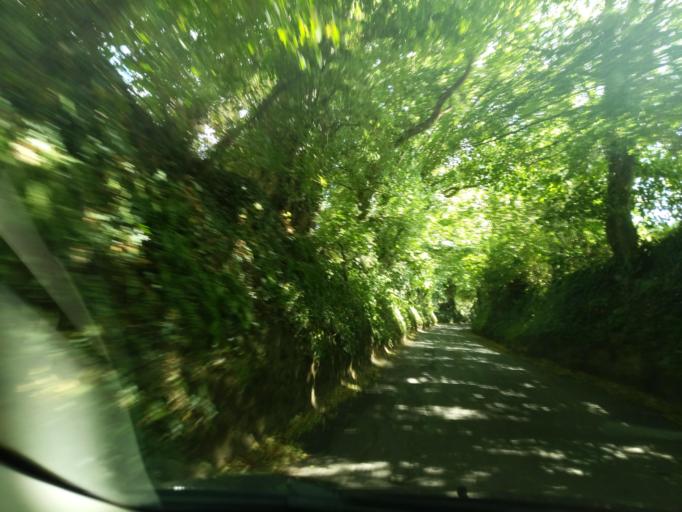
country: GB
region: England
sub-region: Devon
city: Modbury
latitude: 50.3634
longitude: -3.8995
